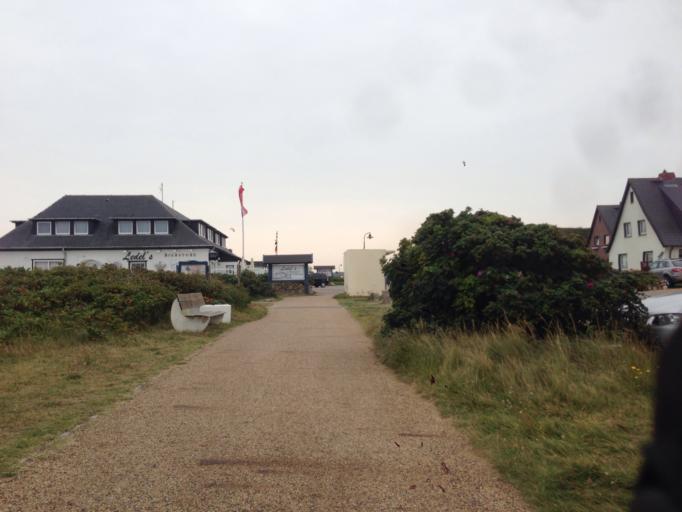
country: DE
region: Schleswig-Holstein
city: Norddorf
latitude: 54.7710
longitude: 8.2865
